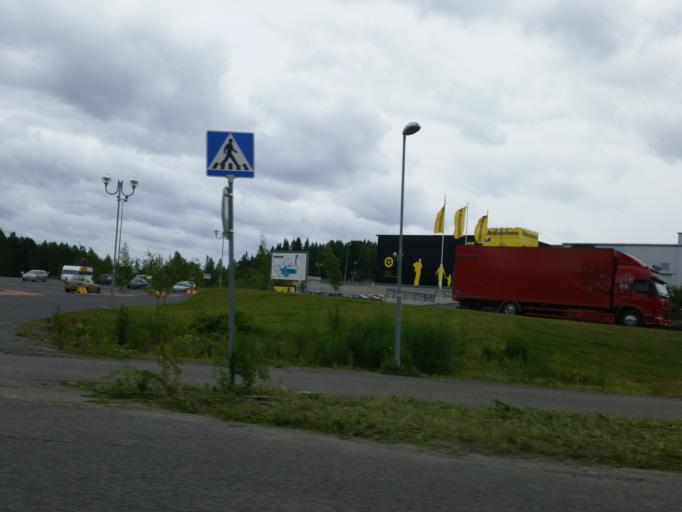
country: FI
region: Northern Savo
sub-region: Kuopio
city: Kuopio
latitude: 62.8750
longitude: 27.6232
